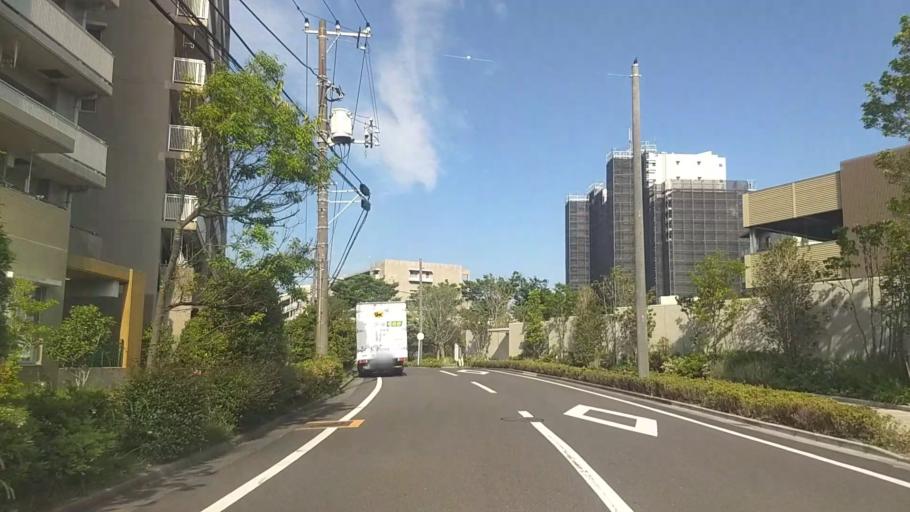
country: JP
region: Kanagawa
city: Fujisawa
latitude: 35.3439
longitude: 139.4919
